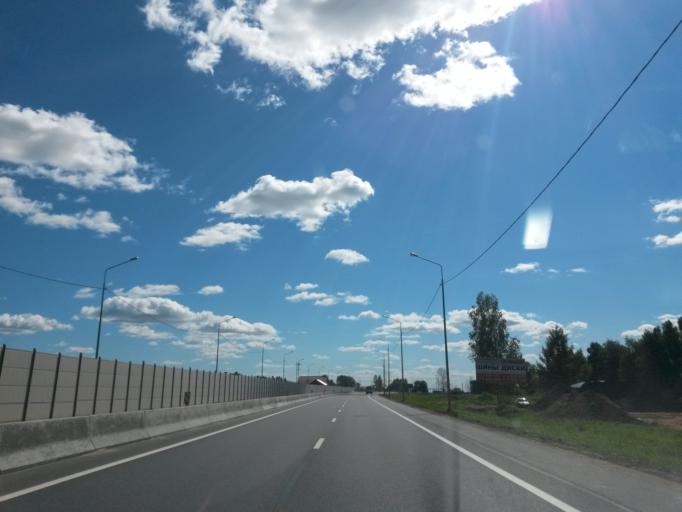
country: RU
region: Jaroslavl
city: Yaroslavl
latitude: 57.7144
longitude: 39.9030
